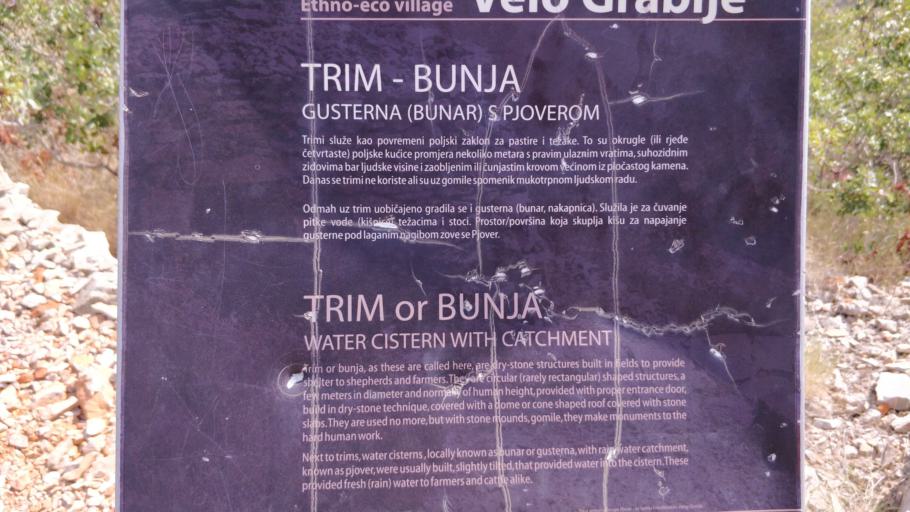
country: HR
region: Splitsko-Dalmatinska
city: Stari Grad
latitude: 43.1753
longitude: 16.5270
